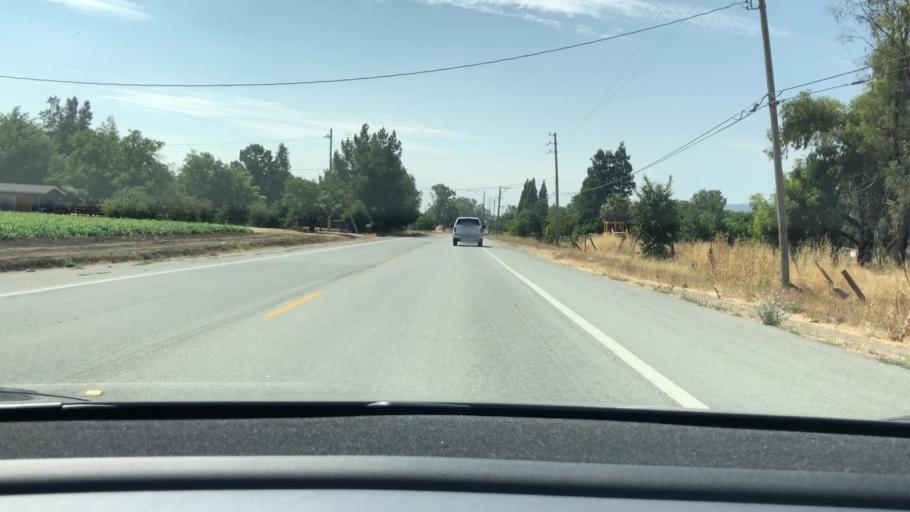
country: US
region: California
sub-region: Santa Clara County
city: San Martin
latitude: 37.0432
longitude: -121.6000
